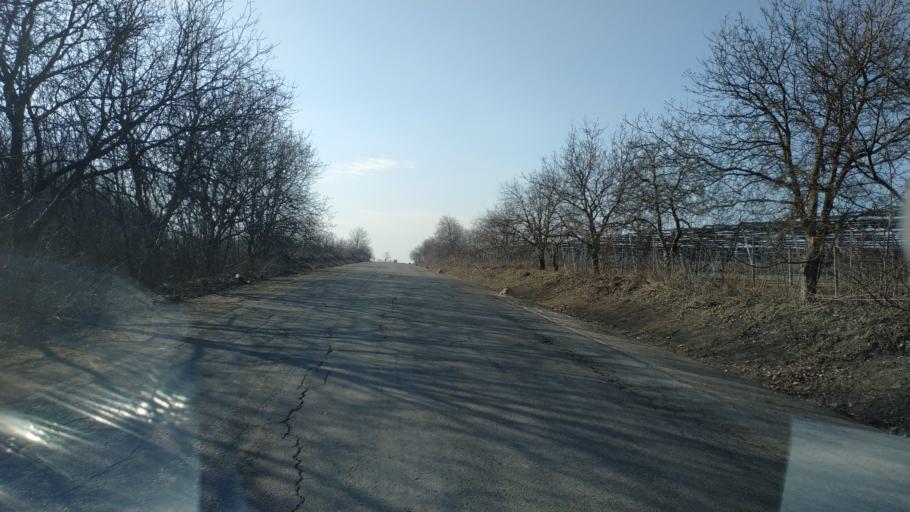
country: MD
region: Chisinau
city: Singera
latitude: 46.8611
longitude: 29.0317
